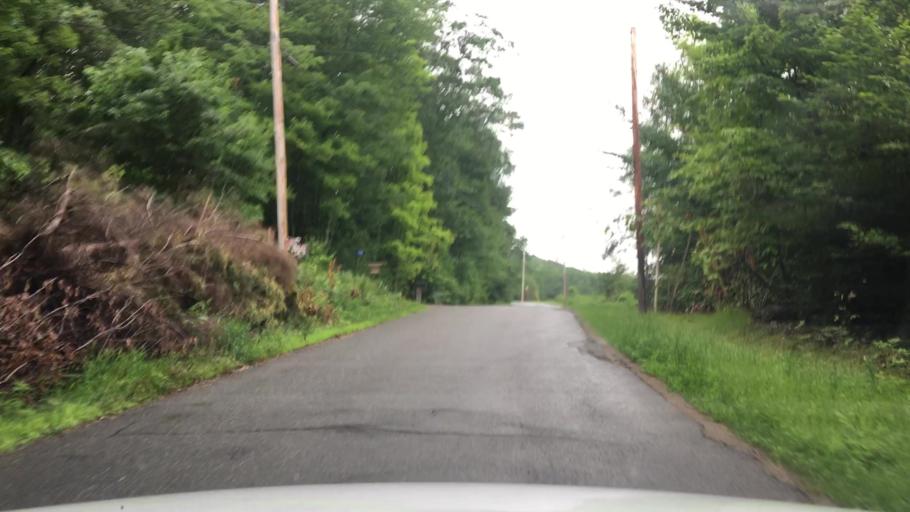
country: US
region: Maine
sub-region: Knox County
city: Hope
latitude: 44.2323
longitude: -69.1792
